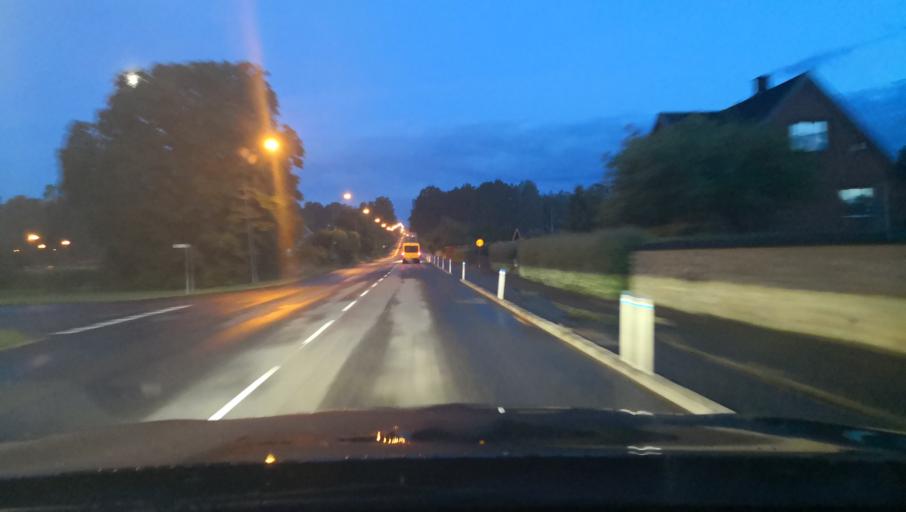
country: SE
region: Skane
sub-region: Osby Kommun
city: Osby
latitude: 56.3683
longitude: 13.9837
